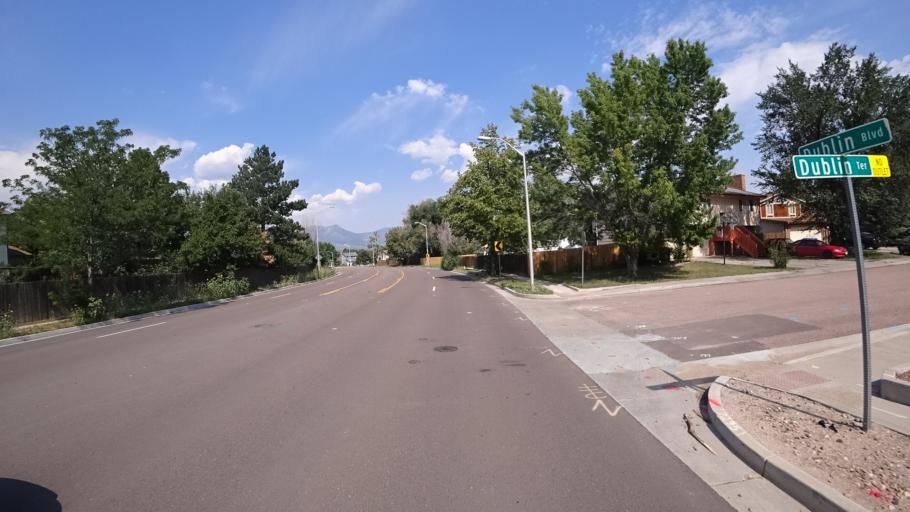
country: US
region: Colorado
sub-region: El Paso County
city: Colorado Springs
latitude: 38.9267
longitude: -104.7865
